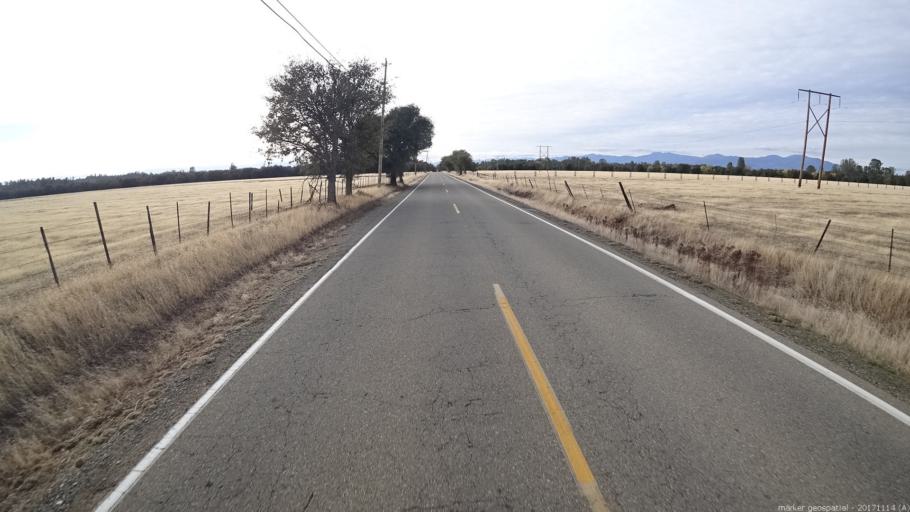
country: US
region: California
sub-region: Shasta County
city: Anderson
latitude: 40.3885
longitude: -122.4158
